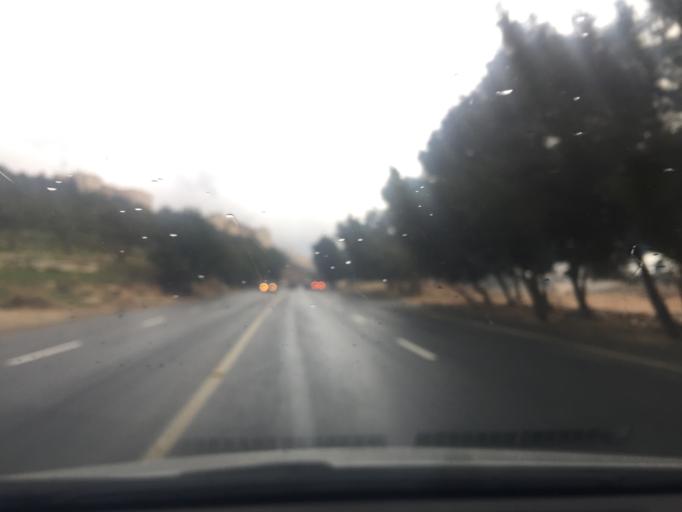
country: JO
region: Amman
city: Amman
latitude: 32.0162
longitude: 35.9354
